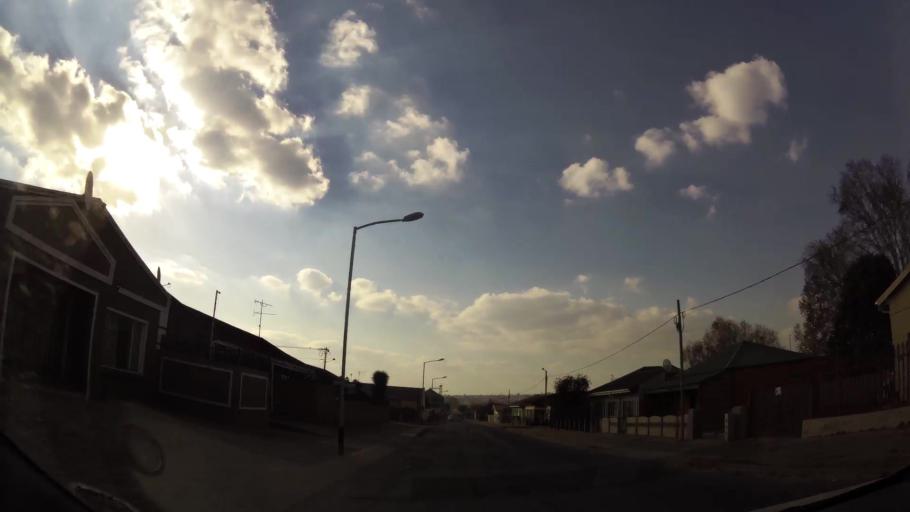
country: ZA
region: Gauteng
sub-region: West Rand District Municipality
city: Krugersdorp
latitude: -26.1009
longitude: 27.7529
